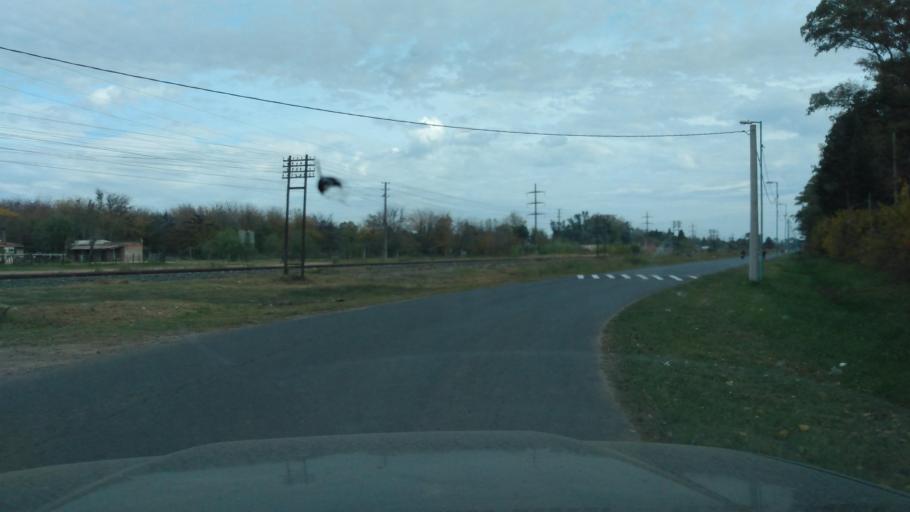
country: AR
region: Buenos Aires
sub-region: Partido de Lujan
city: Lujan
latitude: -34.5853
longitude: -59.1285
